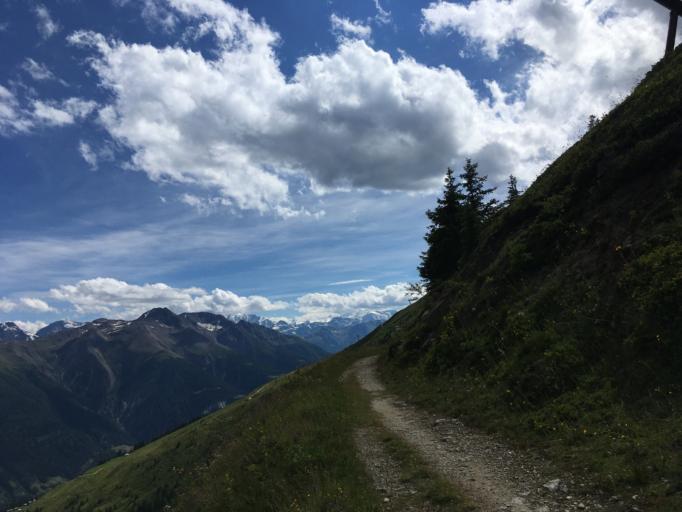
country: CH
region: Valais
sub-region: Goms District
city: Fiesch
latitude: 46.4266
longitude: 8.1168
